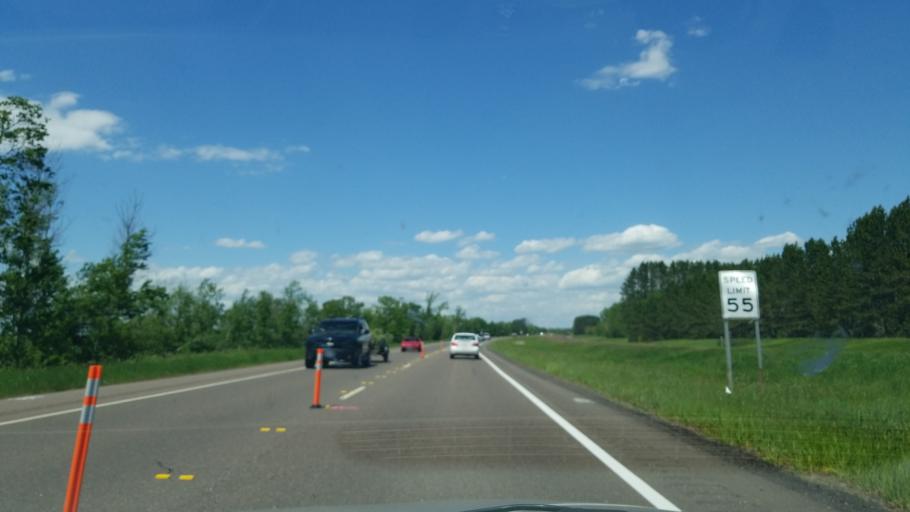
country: US
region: Minnesota
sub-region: Pine County
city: Sandstone
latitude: 46.2718
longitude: -92.8253
